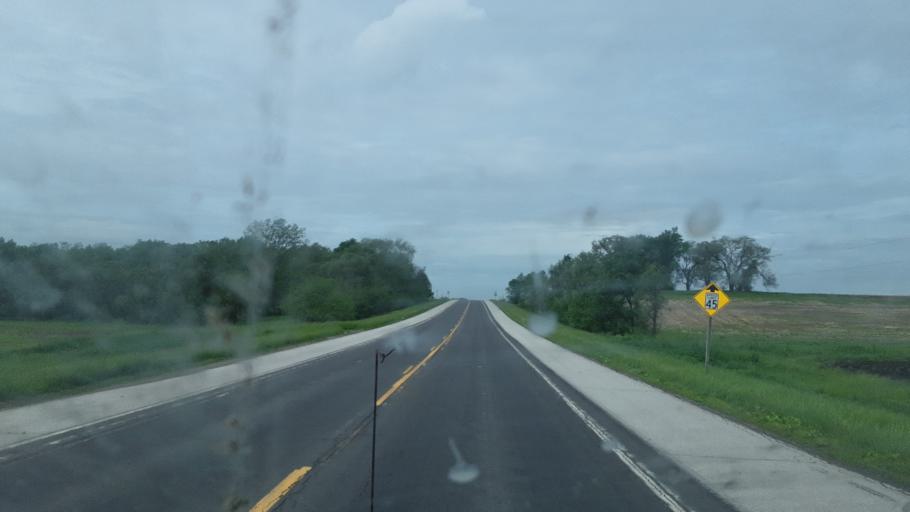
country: US
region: Illinois
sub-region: Hancock County
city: Warsaw
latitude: 40.3949
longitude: -91.5611
